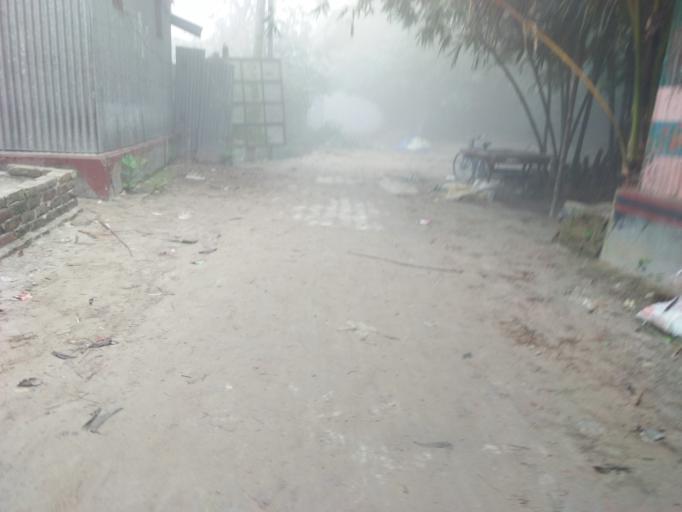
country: BD
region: Dhaka
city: Azimpur
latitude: 23.6883
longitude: 90.3000
